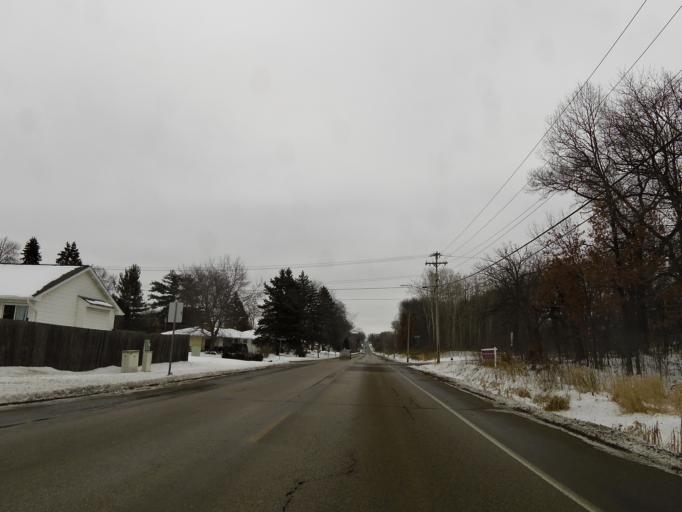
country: US
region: Minnesota
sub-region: Ramsey County
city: North Saint Paul
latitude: 45.0064
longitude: -93.0134
